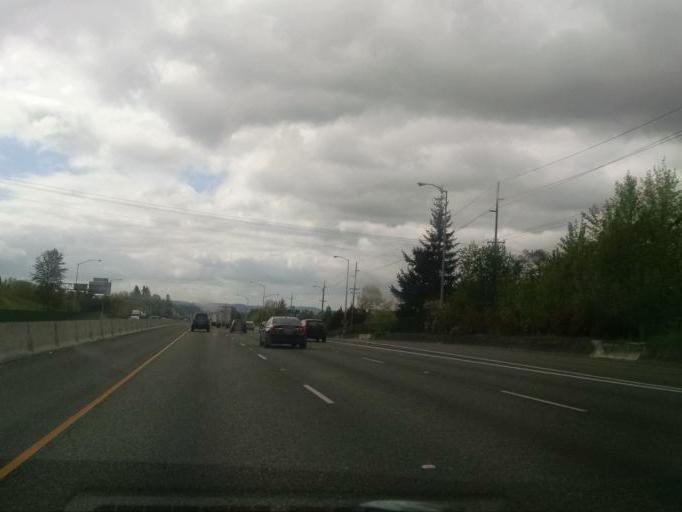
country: US
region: Oregon
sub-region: Washington County
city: Metzger
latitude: 45.4366
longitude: -122.7443
